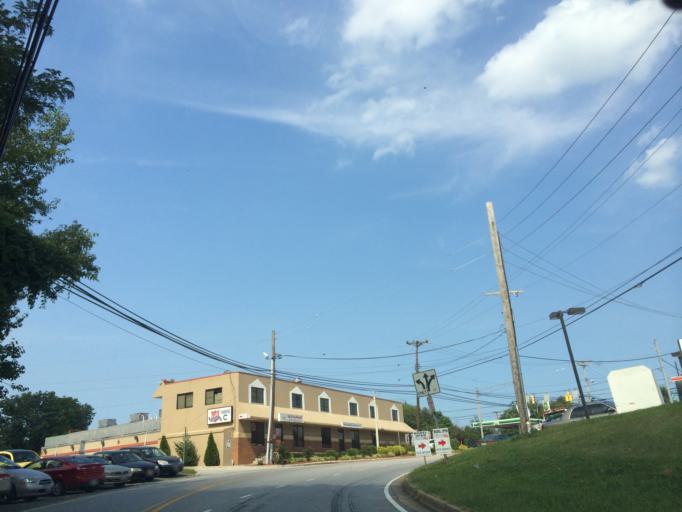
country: US
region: Maryland
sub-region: Baltimore County
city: Lansdowne
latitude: 39.2243
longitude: -76.6666
